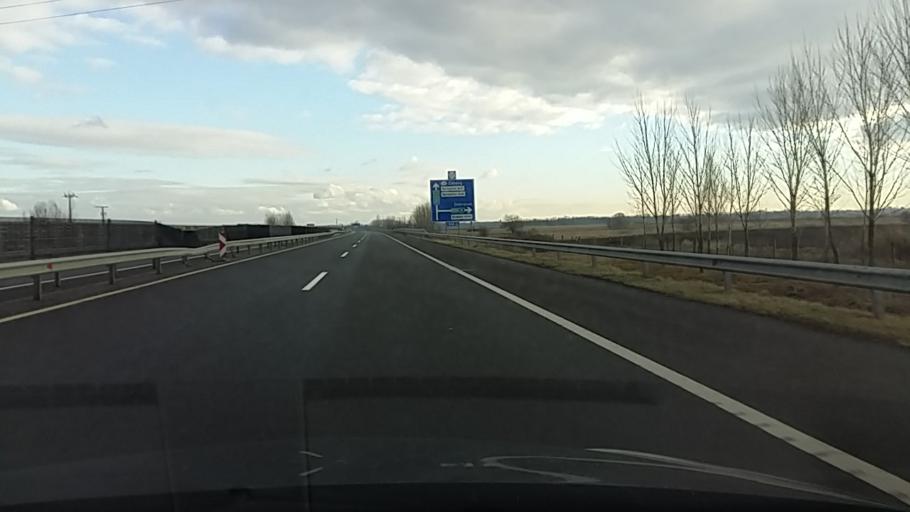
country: HU
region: Szabolcs-Szatmar-Bereg
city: Nyiregyhaza
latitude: 47.8895
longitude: 21.6931
